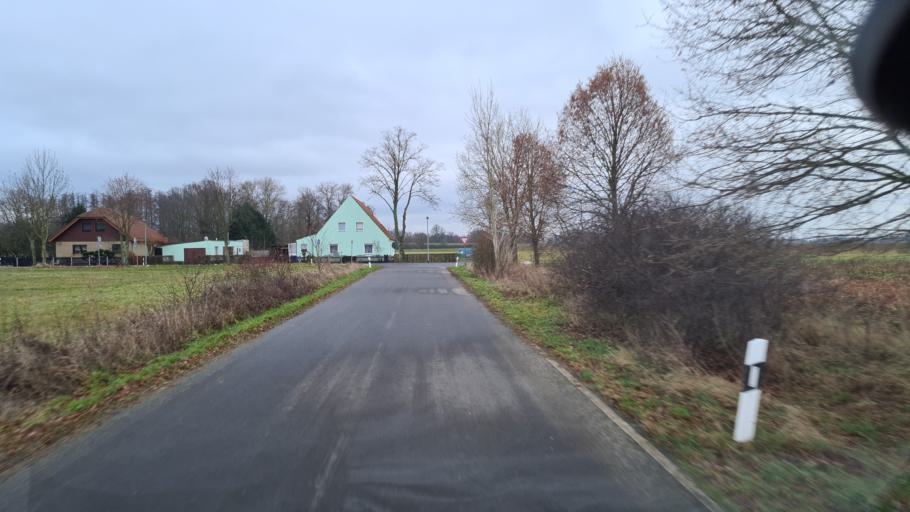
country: DE
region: Brandenburg
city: Vogelsang
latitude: 52.2396
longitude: 14.6973
